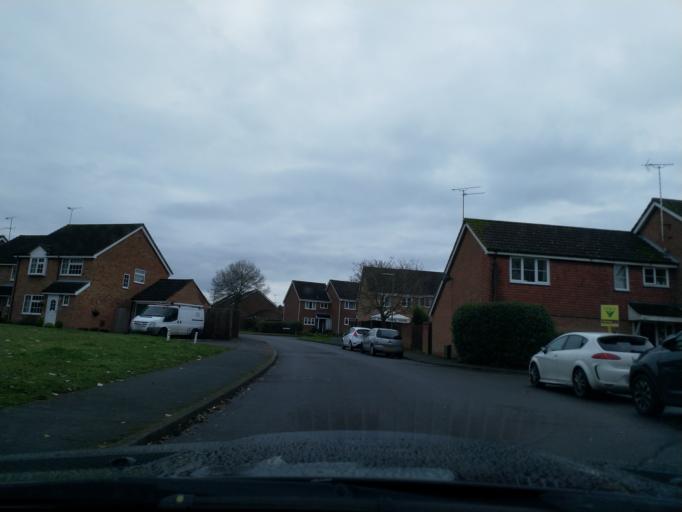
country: GB
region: England
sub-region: Surrey
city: Frimley
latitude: 51.3120
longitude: -0.7271
